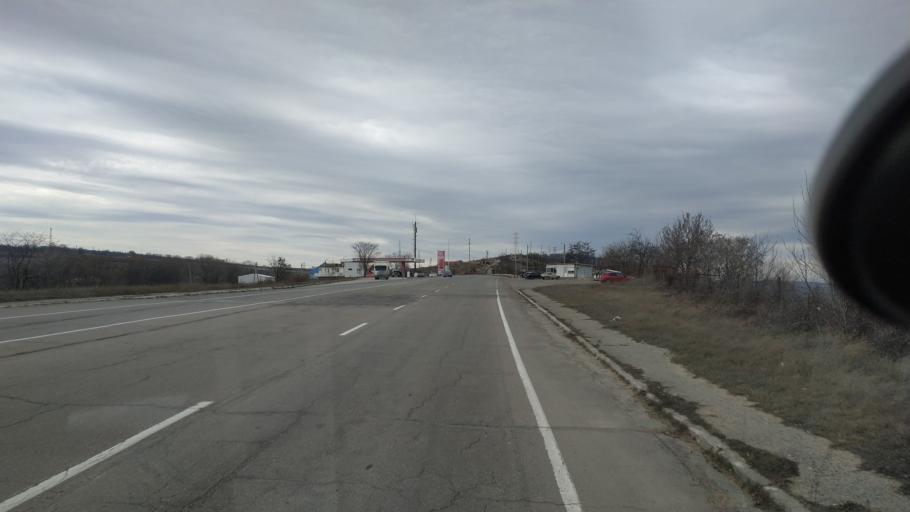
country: MD
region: Chisinau
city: Vadul lui Voda
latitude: 47.0870
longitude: 29.0734
